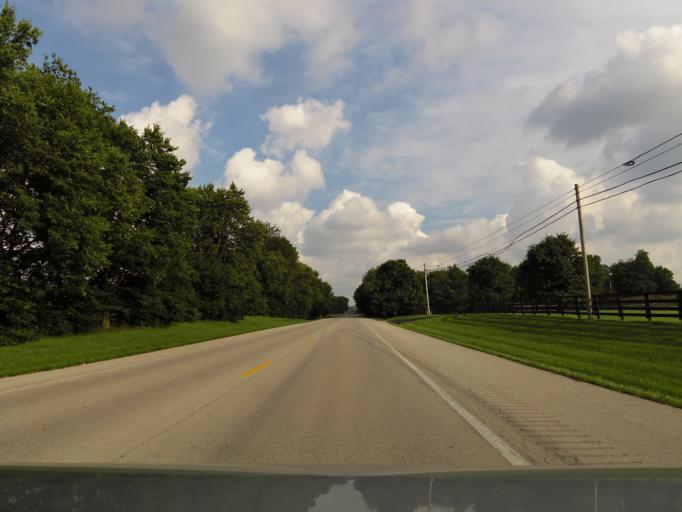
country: US
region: Kentucky
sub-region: Bourbon County
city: Paris
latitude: 38.2557
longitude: -84.2915
